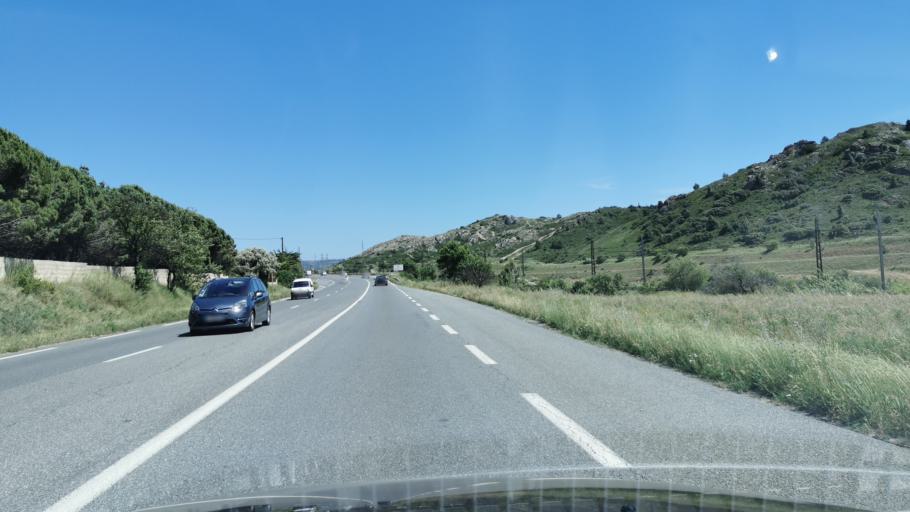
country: FR
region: Languedoc-Roussillon
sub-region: Departement de l'Aude
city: Narbonne
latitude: 43.1814
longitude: 2.9547
